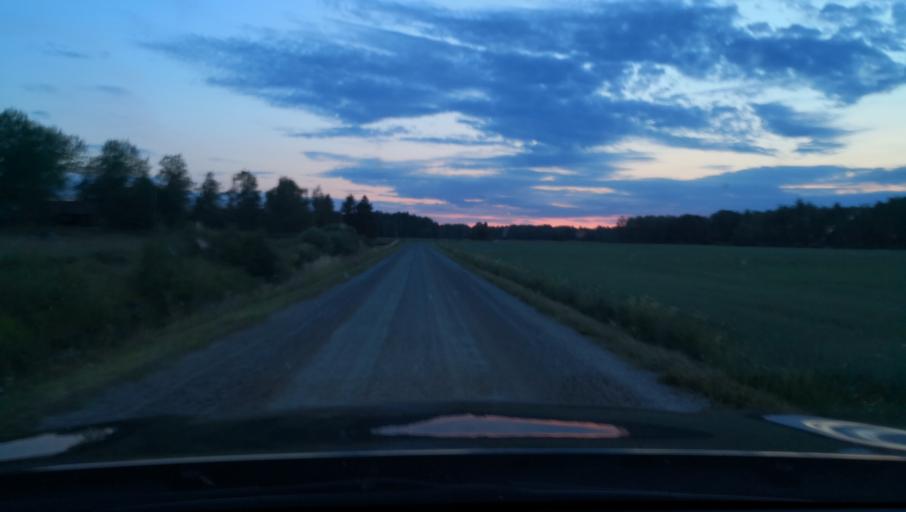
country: SE
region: Uppsala
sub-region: Heby Kommun
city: OEstervala
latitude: 60.0123
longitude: 17.3146
